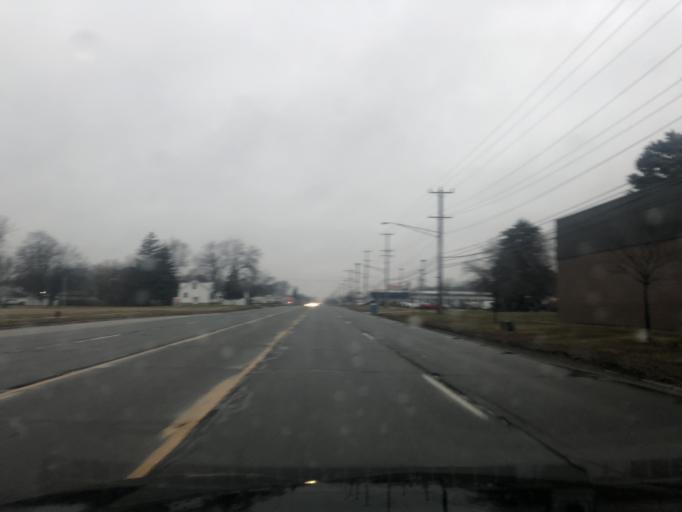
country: US
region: Michigan
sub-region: Wayne County
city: Taylor
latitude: 42.2690
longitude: -83.2782
